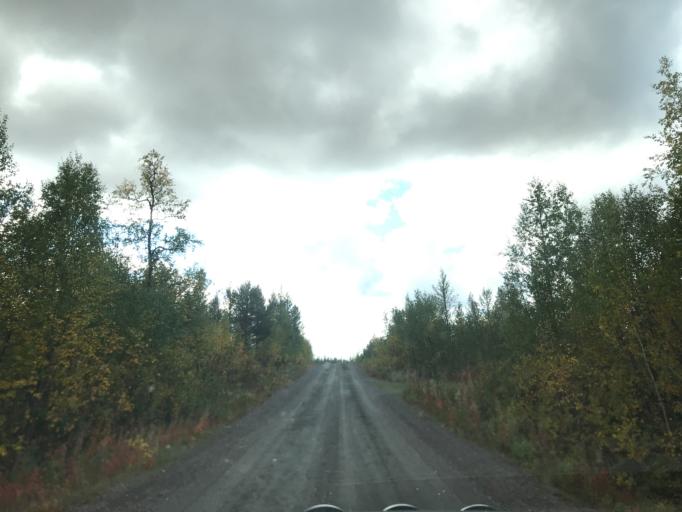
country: SE
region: Norrbotten
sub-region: Gallivare Kommun
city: Malmberget
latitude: 67.5889
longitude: 20.8752
